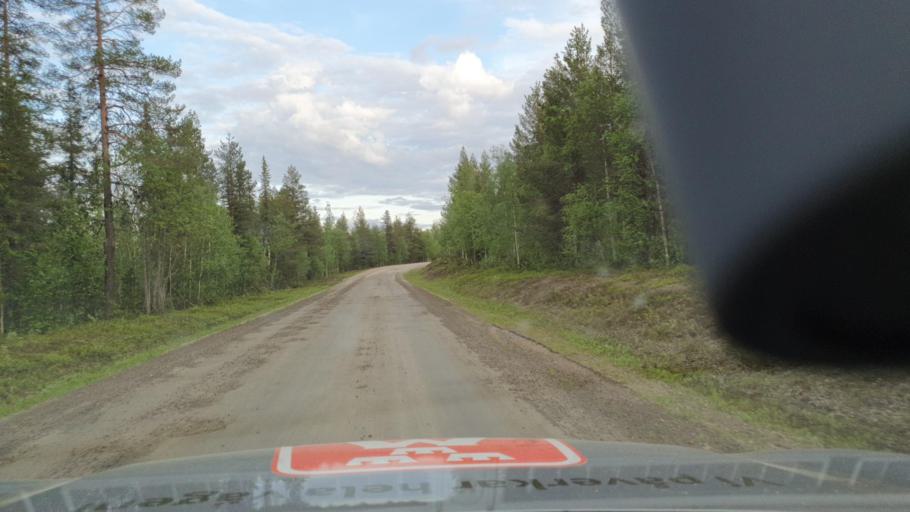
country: SE
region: Norrbotten
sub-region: Gallivare Kommun
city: Gaellivare
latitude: 66.7201
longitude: 21.1515
